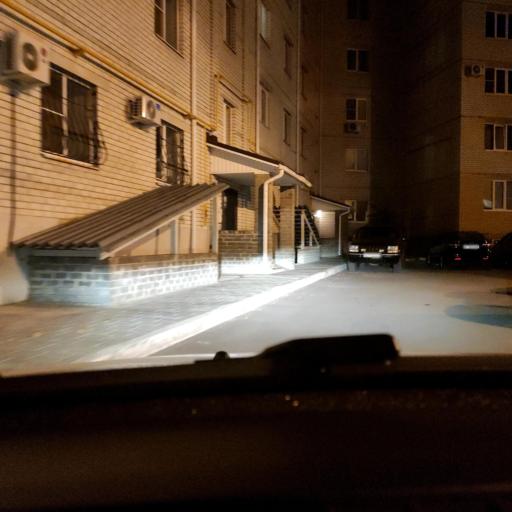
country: RU
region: Voronezj
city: Voronezh
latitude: 51.6502
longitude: 39.1808
